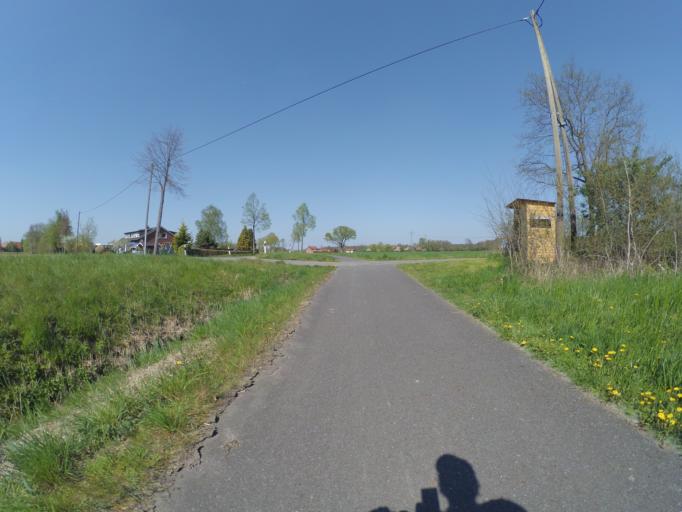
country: DE
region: North Rhine-Westphalia
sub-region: Regierungsbezirk Munster
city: Ascheberg
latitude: 51.8625
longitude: 7.5941
